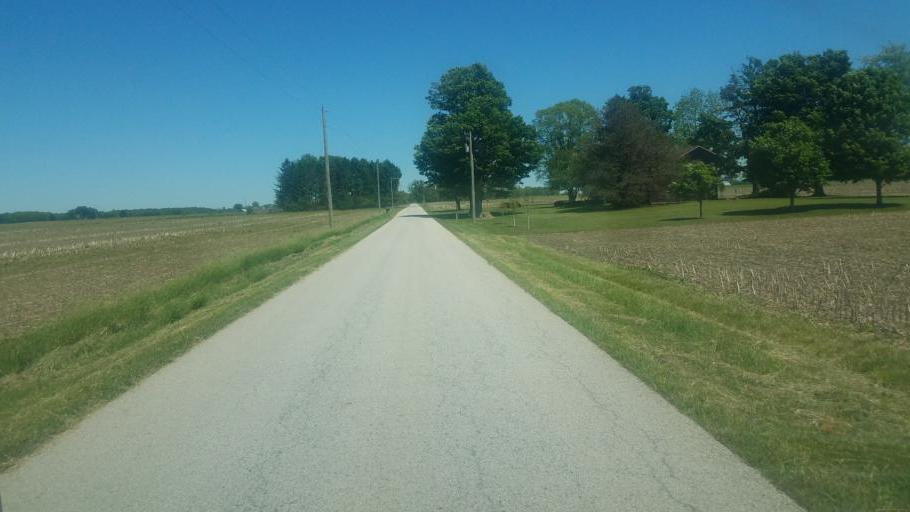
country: US
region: Ohio
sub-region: Champaign County
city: Saint Paris
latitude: 40.1995
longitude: -84.0464
